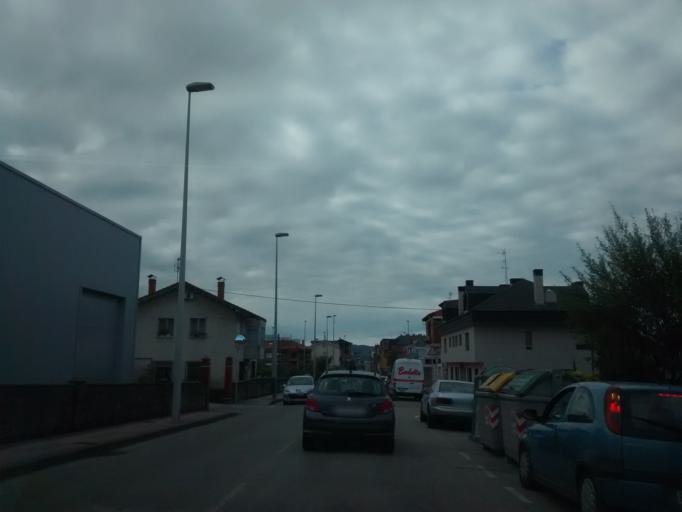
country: ES
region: Cantabria
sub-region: Provincia de Cantabria
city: Torrelavega
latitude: 43.3450
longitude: -4.0373
